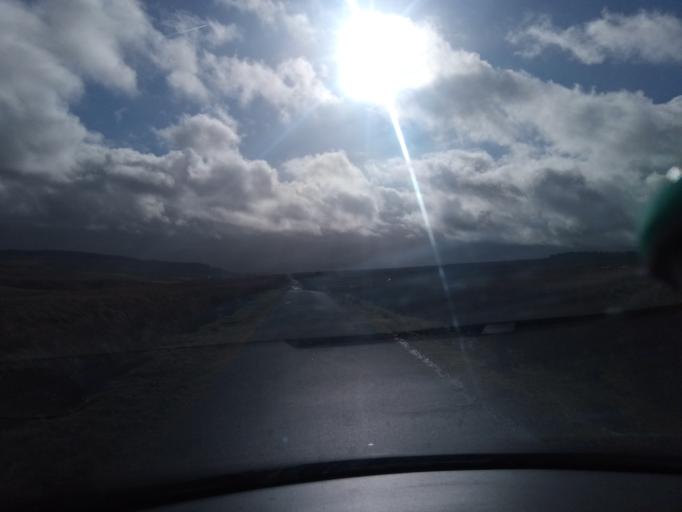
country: GB
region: England
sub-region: Northumberland
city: Rochester
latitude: 55.3153
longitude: -2.2875
